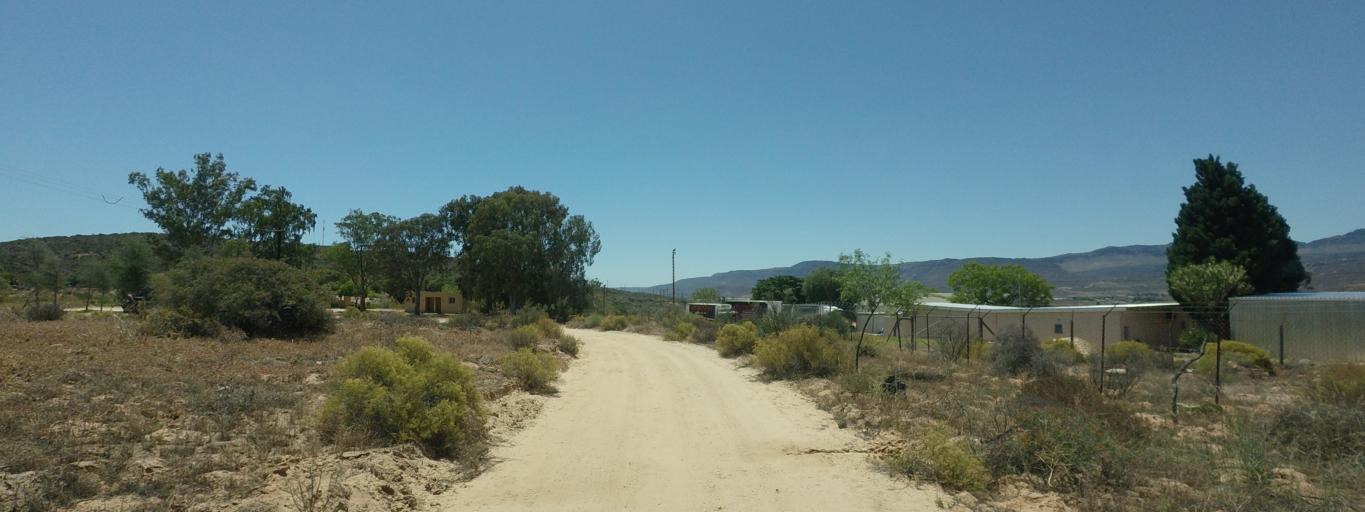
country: ZA
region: Western Cape
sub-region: West Coast District Municipality
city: Clanwilliam
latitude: -32.1872
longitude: 18.8846
